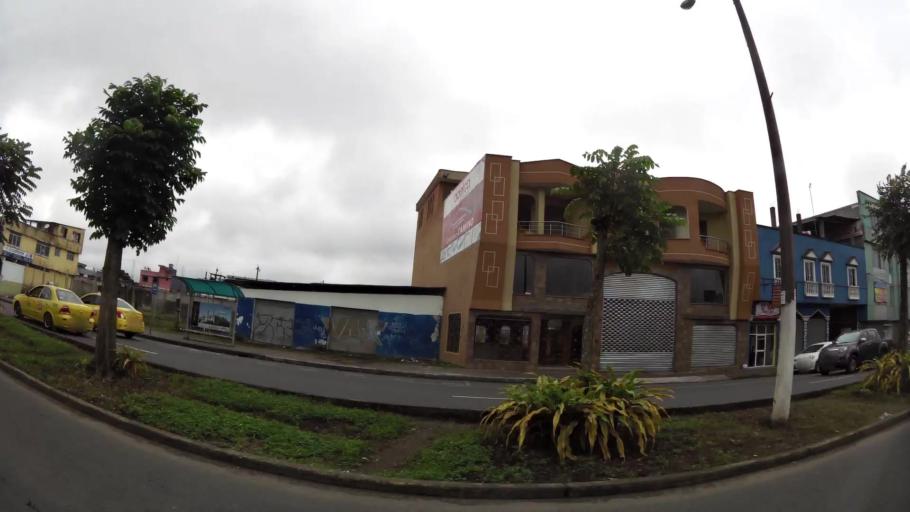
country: EC
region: Santo Domingo de los Tsachilas
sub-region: Canton Santo Domingo de los Colorados
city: Santo Domingo de los Colorados
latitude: -0.2616
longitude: -79.1612
